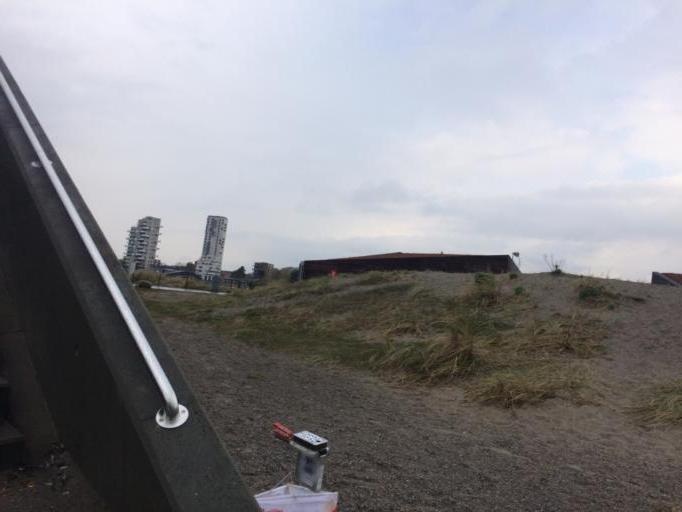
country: DK
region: Capital Region
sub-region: Kobenhavn
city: Christianshavn
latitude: 55.6633
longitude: 12.6390
